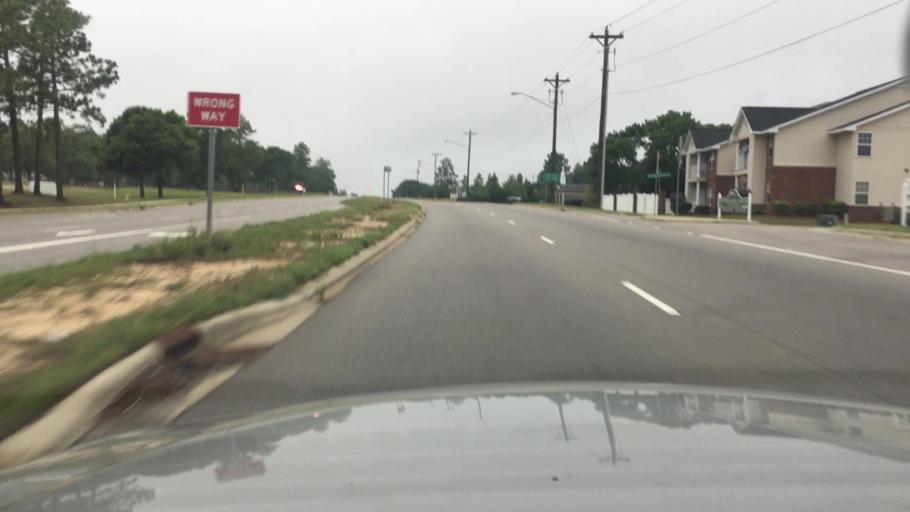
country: US
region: North Carolina
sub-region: Cumberland County
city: Hope Mills
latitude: 34.9786
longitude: -78.9244
